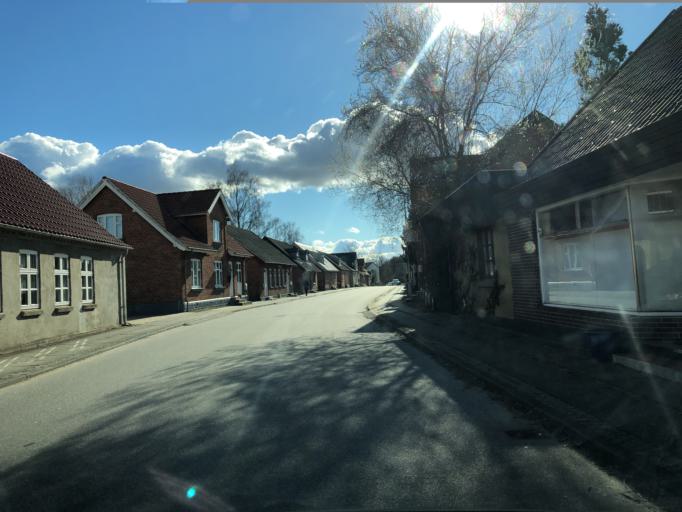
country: DK
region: Central Jutland
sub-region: Favrskov Kommune
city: Hinnerup
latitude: 56.2629
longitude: 10.0615
